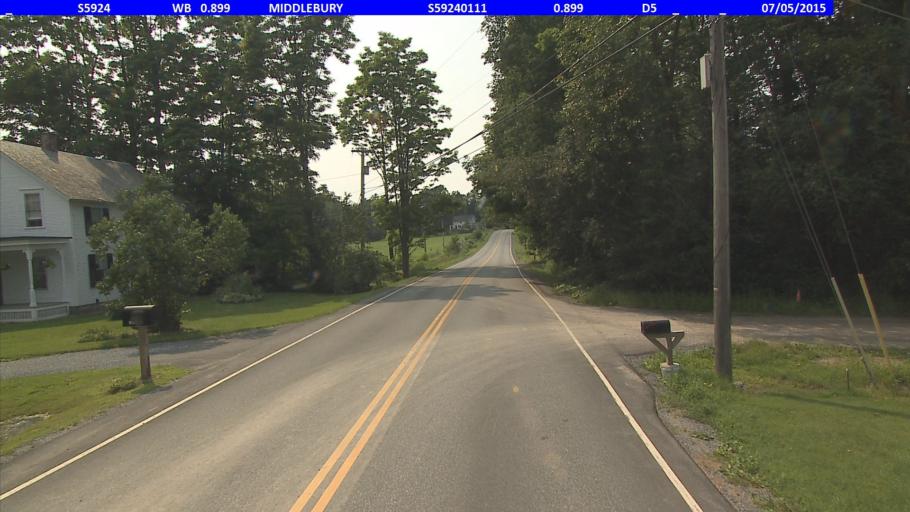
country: US
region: Vermont
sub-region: Addison County
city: Middlebury (village)
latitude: 44.0127
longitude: -73.1447
